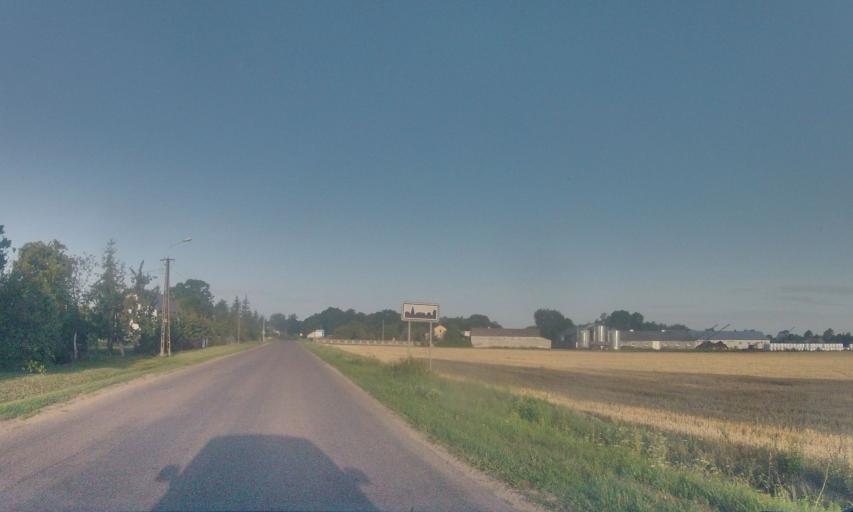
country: PL
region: Masovian Voivodeship
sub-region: Powiat mlawski
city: Szrensk
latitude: 52.9962
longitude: 20.2108
